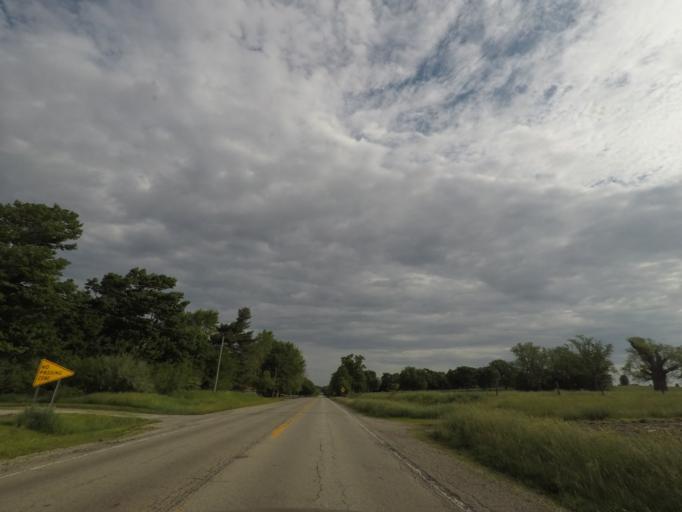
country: US
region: Illinois
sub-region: Logan County
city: Mount Pulaski
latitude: 40.0453
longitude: -89.2822
